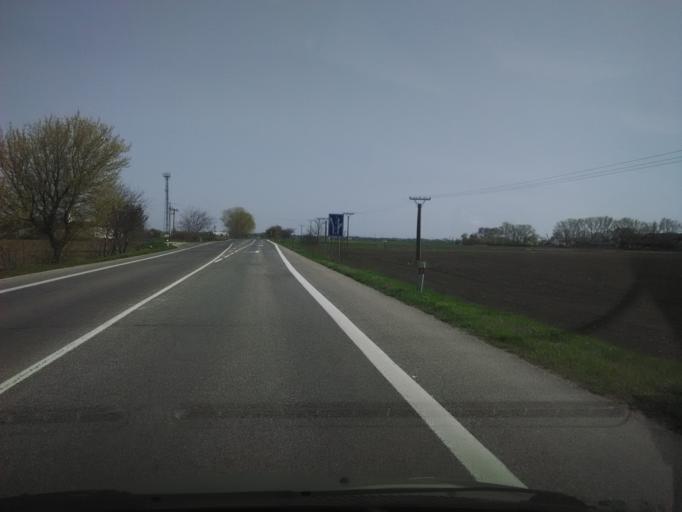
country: SK
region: Trnavsky
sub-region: Okres Galanta
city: Galanta
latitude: 48.1806
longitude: 17.7881
